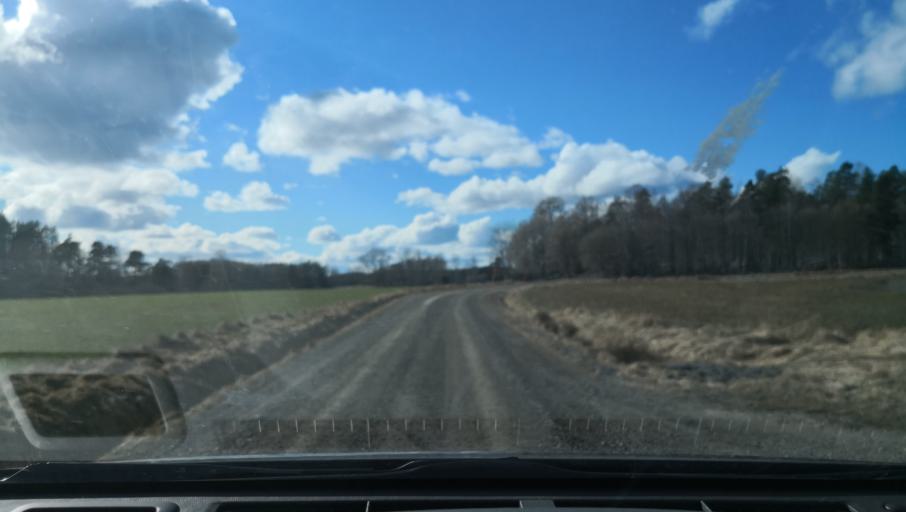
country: SE
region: OErebro
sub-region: Lindesbergs Kommun
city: Fellingsbro
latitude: 59.4211
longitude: 15.6953
